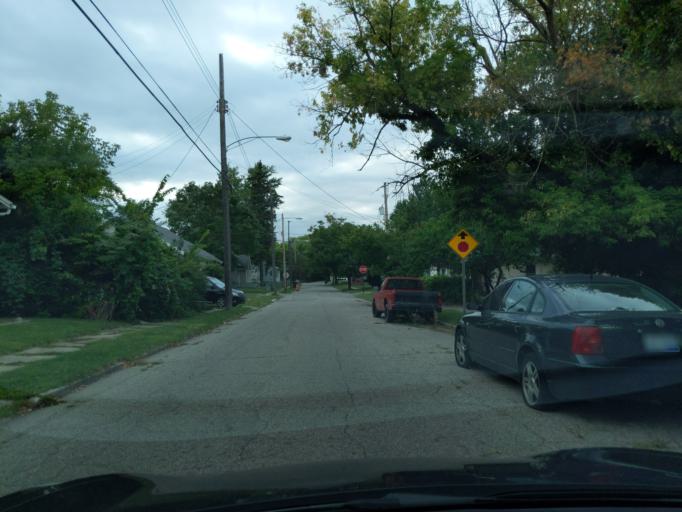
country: US
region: Michigan
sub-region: Ingham County
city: Lansing
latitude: 42.7240
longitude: -84.5311
